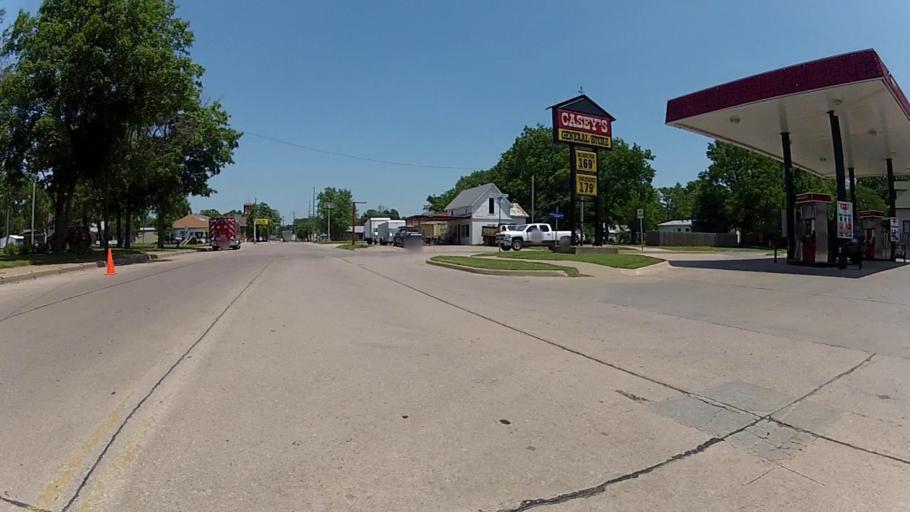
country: US
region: Kansas
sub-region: Montgomery County
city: Cherryvale
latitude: 37.2654
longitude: -95.5555
